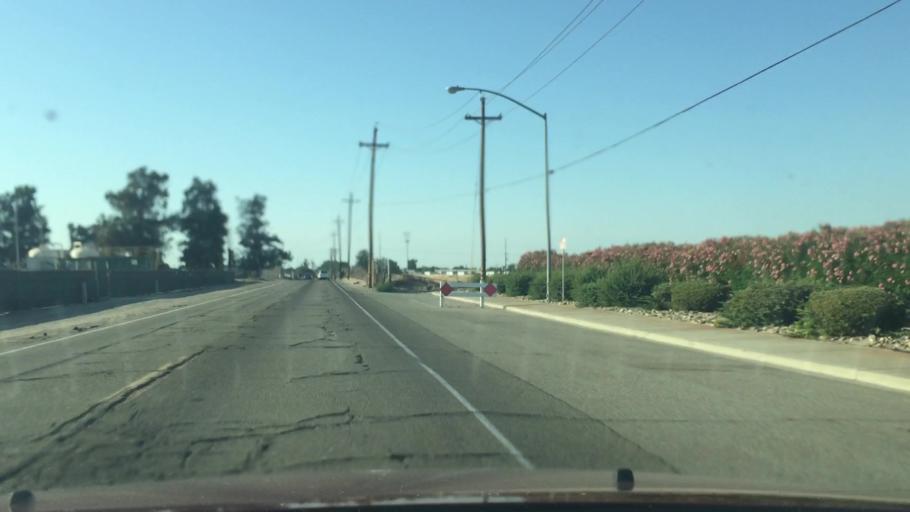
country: US
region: California
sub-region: San Joaquin County
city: Lathrop
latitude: 37.8077
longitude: -121.2711
